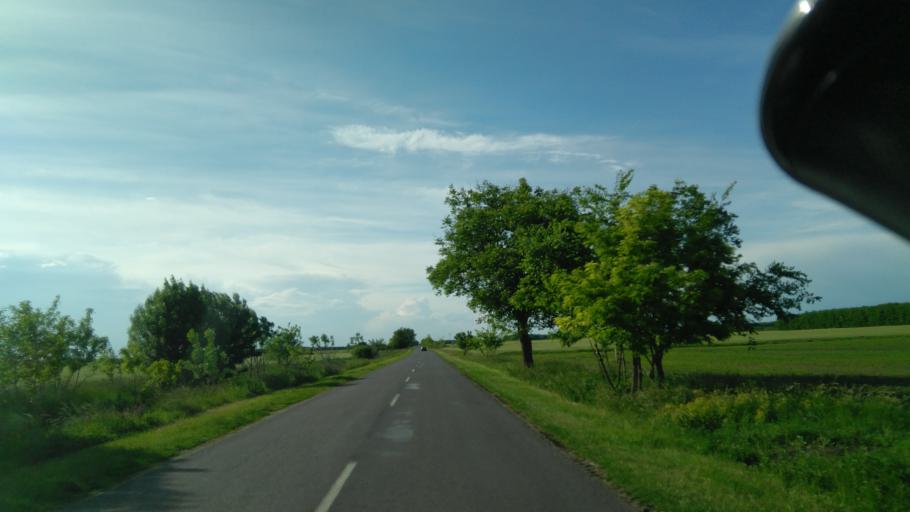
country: HU
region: Bekes
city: Lokoshaza
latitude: 46.4431
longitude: 21.2228
